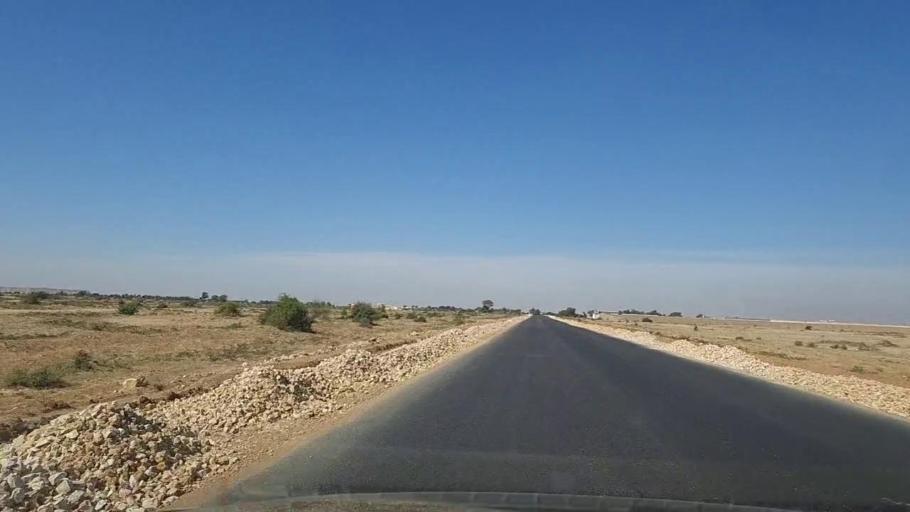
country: PK
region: Sindh
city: Kotri
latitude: 25.2767
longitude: 68.2142
